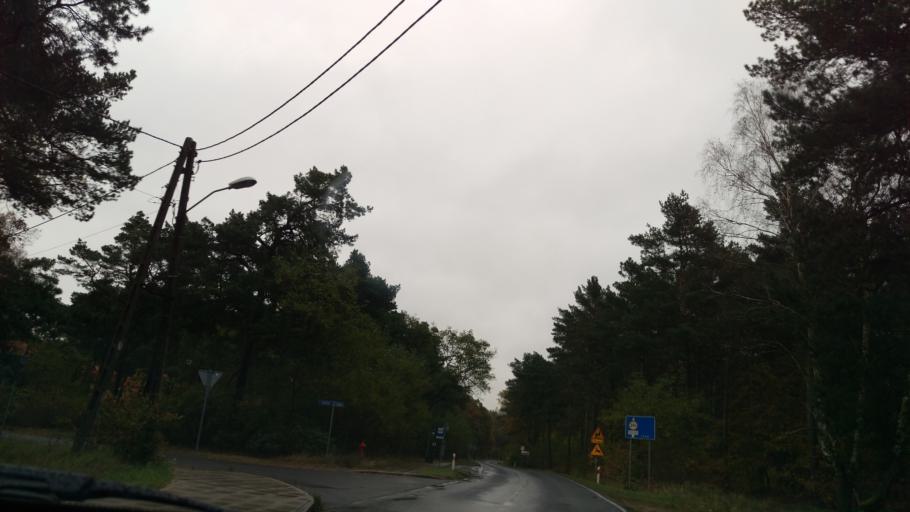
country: PL
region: West Pomeranian Voivodeship
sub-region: Szczecin
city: Szczecin
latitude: 53.3970
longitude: 14.6911
